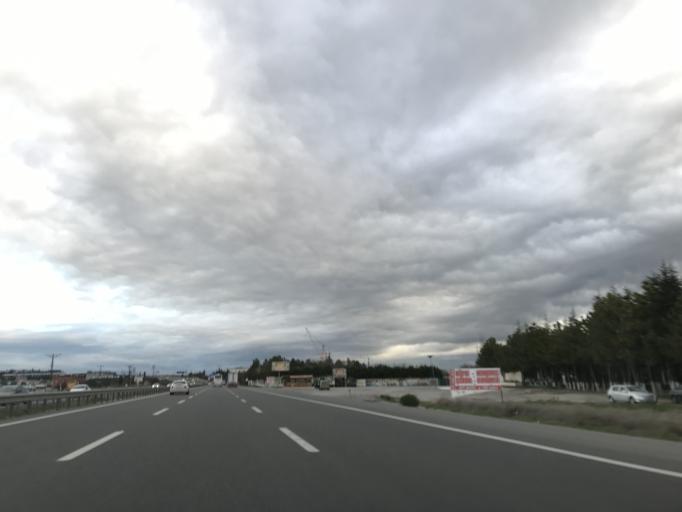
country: TR
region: Ankara
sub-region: Goelbasi
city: Golbasi
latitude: 39.7493
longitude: 32.8042
